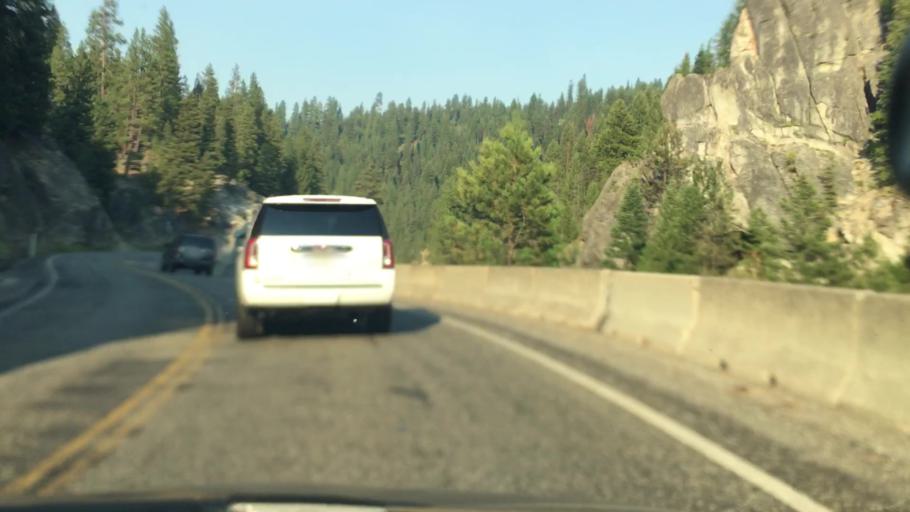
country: US
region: Idaho
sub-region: Valley County
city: Cascade
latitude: 44.3120
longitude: -116.0773
